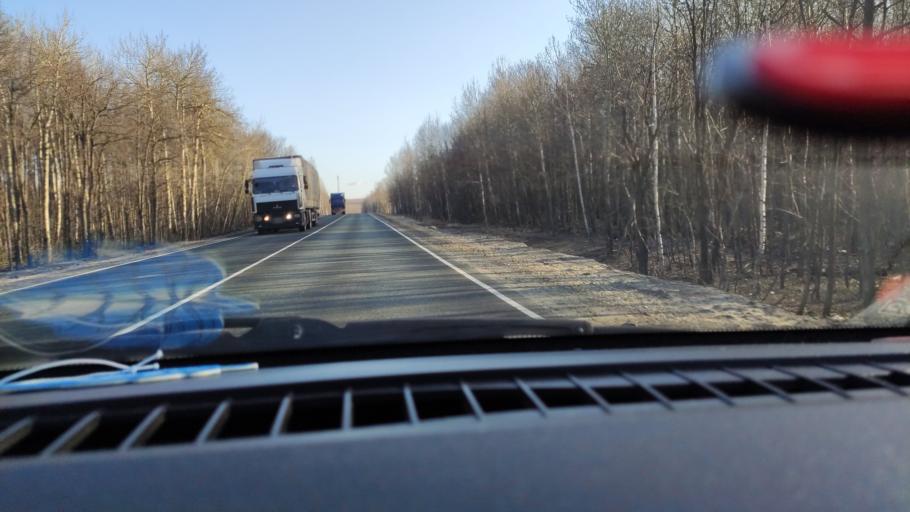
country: RU
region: Saratov
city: Khvalynsk
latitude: 52.4536
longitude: 48.0136
